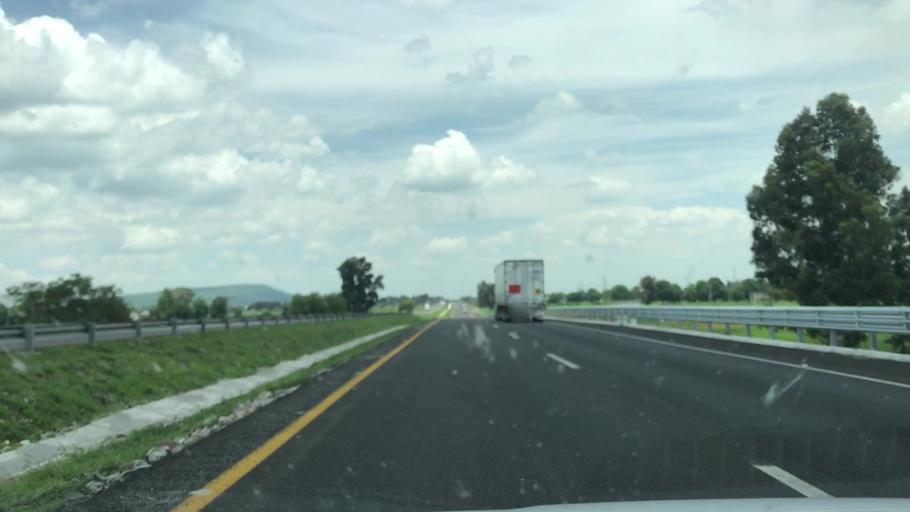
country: MX
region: Guanajuato
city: Salamanca
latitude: 20.6020
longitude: -101.1990
